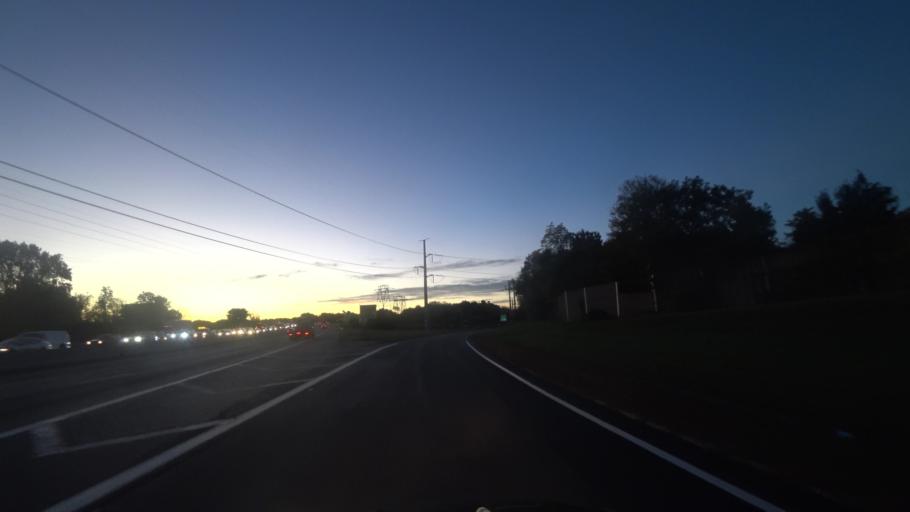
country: US
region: Massachusetts
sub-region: Essex County
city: Lynnfield
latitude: 42.5144
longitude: -71.0455
